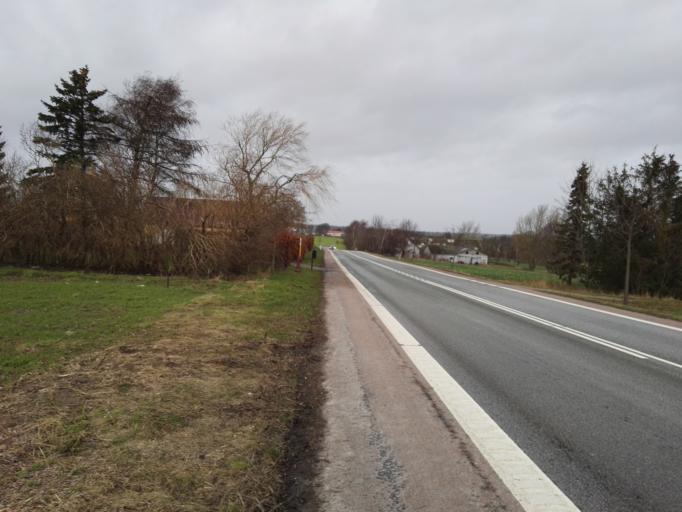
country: DK
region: Capital Region
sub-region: Frederikssund Kommune
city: Skibby
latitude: 55.6788
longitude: 11.9284
